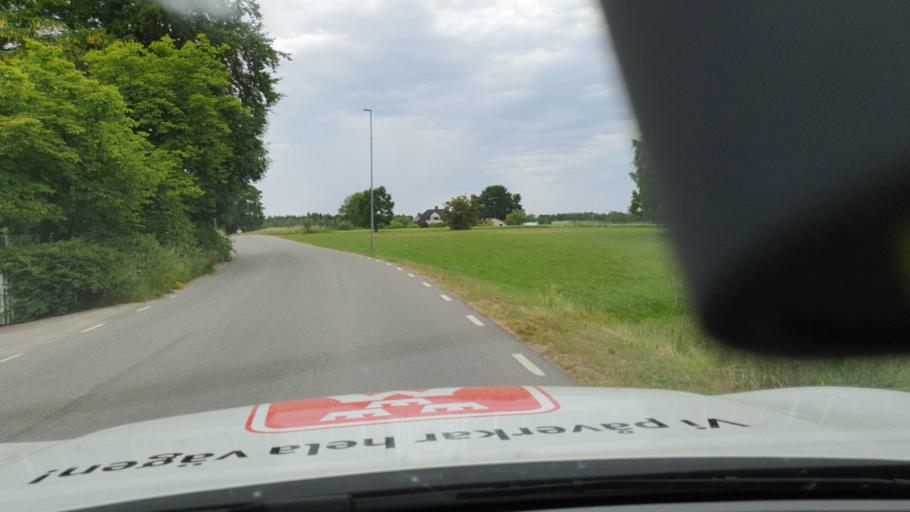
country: SE
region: Vaestra Goetaland
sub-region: Hjo Kommun
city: Hjo
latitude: 58.3121
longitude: 14.3040
